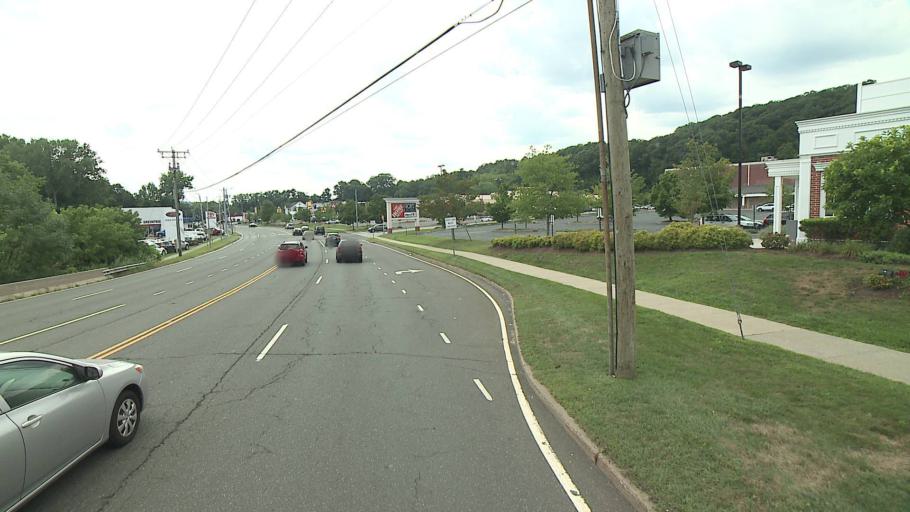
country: US
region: Connecticut
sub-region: Fairfield County
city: Danbury
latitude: 41.4260
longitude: -73.4194
